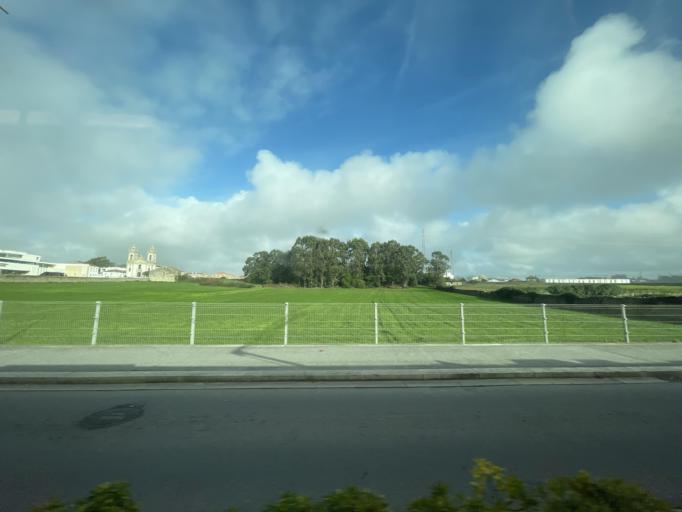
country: PT
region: Porto
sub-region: Vila do Conde
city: Vila do Conde
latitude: 41.3580
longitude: -8.7388
